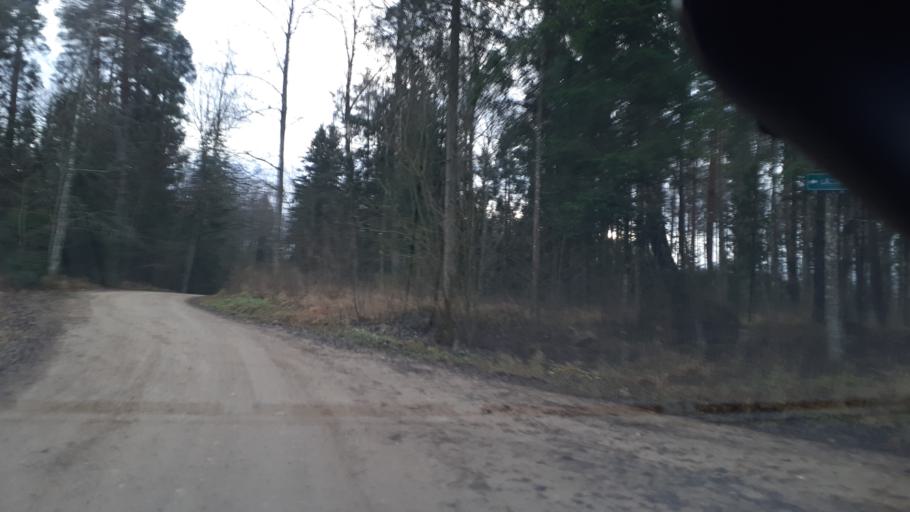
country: LV
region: Kuldigas Rajons
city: Kuldiga
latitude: 56.9017
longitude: 21.9090
